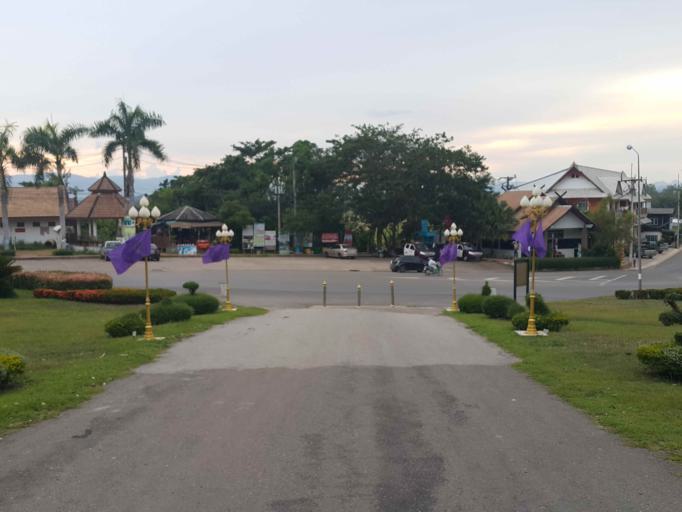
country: TH
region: Nan
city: Phu Phiang
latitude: 18.7589
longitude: 100.7900
